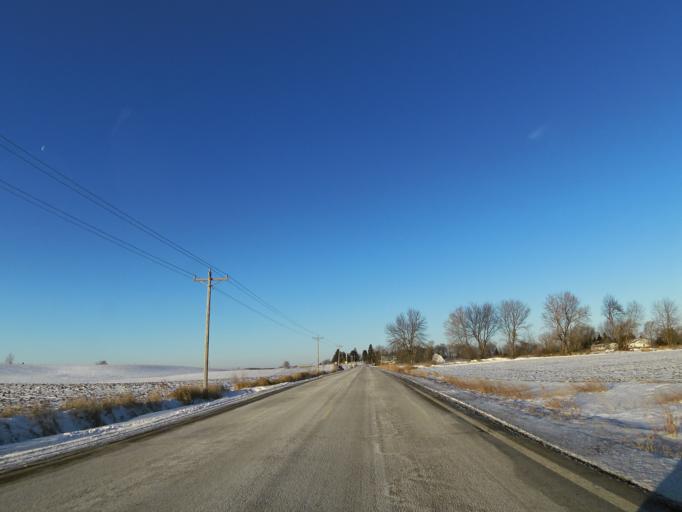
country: US
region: Minnesota
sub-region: Scott County
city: Prior Lake
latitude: 44.6524
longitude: -93.4739
